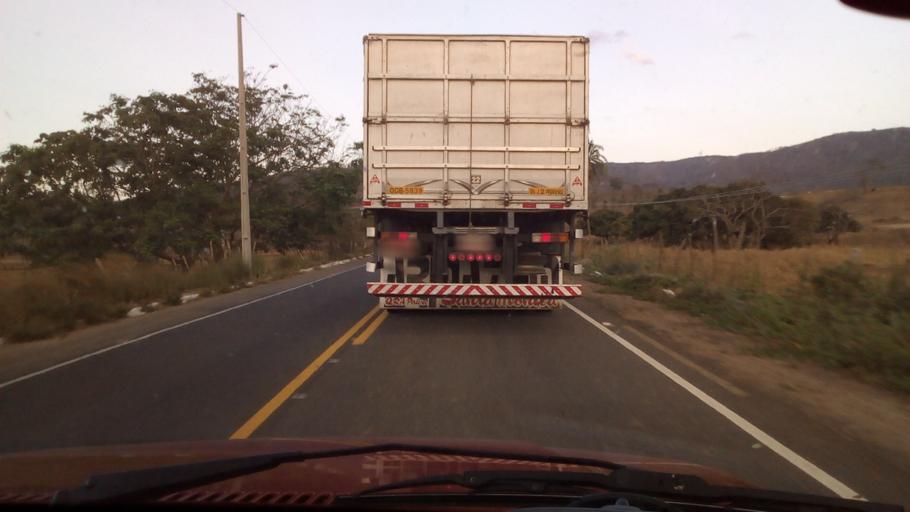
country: BR
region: Paraiba
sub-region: Bananeiras
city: Solanea
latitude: -6.7228
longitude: -35.5497
